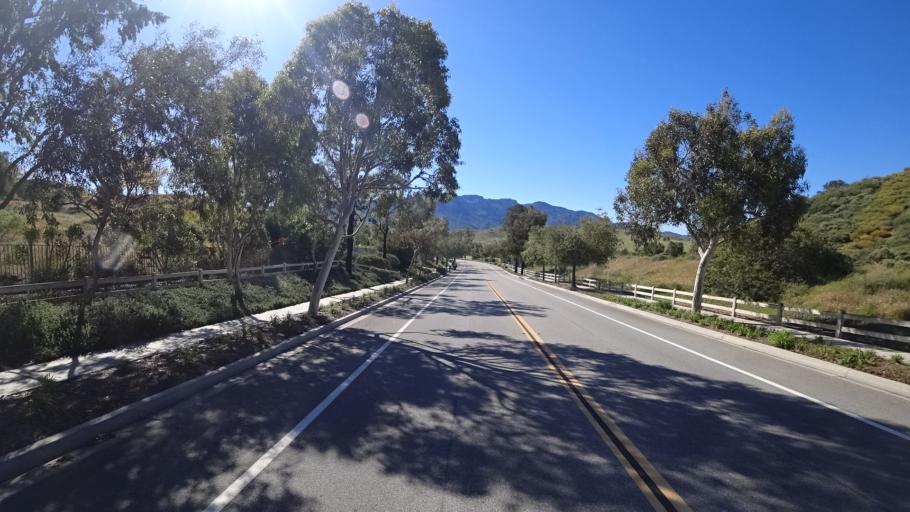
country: US
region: California
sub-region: Ventura County
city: Casa Conejo
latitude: 34.1603
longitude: -118.9872
